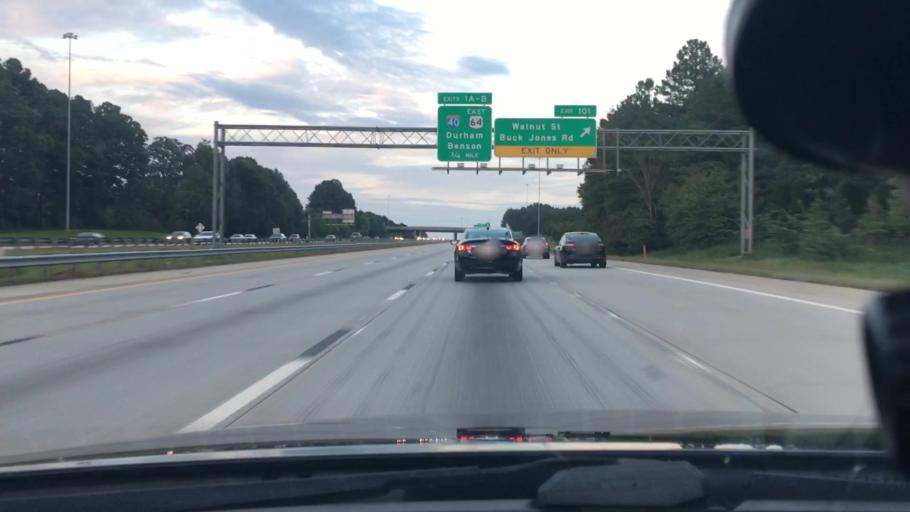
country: US
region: North Carolina
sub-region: Wake County
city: Cary
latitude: 35.7592
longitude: -78.7503
